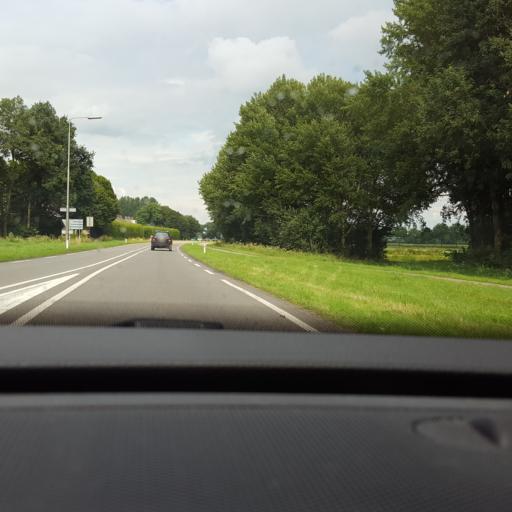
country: NL
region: Gelderland
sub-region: Gemeente Rheden
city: De Steeg
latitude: 51.9914
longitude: 6.0679
